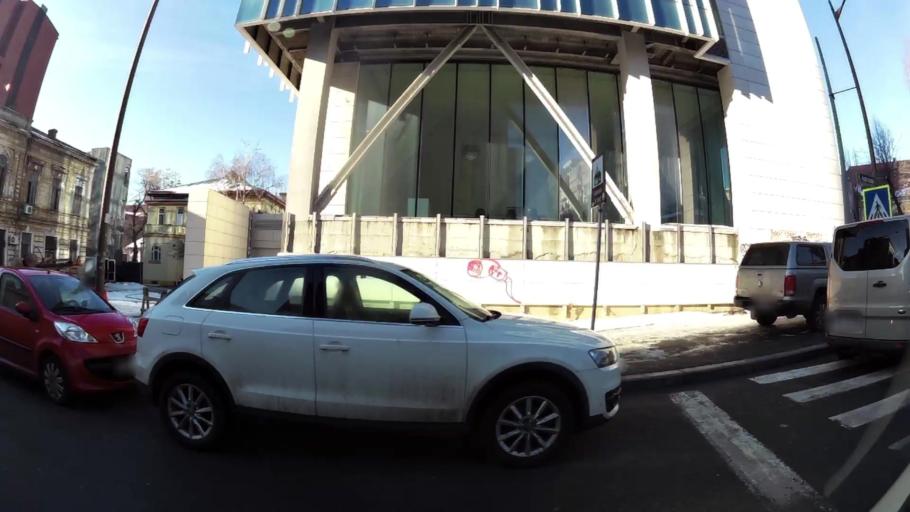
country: RO
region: Bucuresti
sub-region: Municipiul Bucuresti
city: Bucuresti
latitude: 44.4419
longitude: 26.0920
